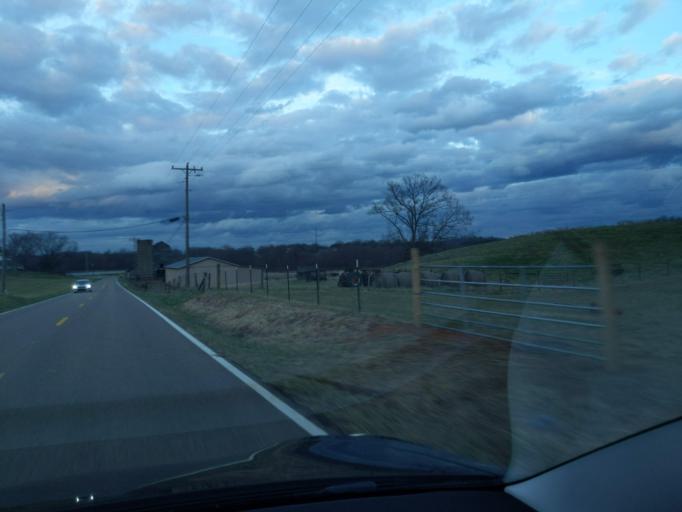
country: US
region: Tennessee
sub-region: Jefferson County
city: Dandridge
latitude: 36.0782
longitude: -83.3793
